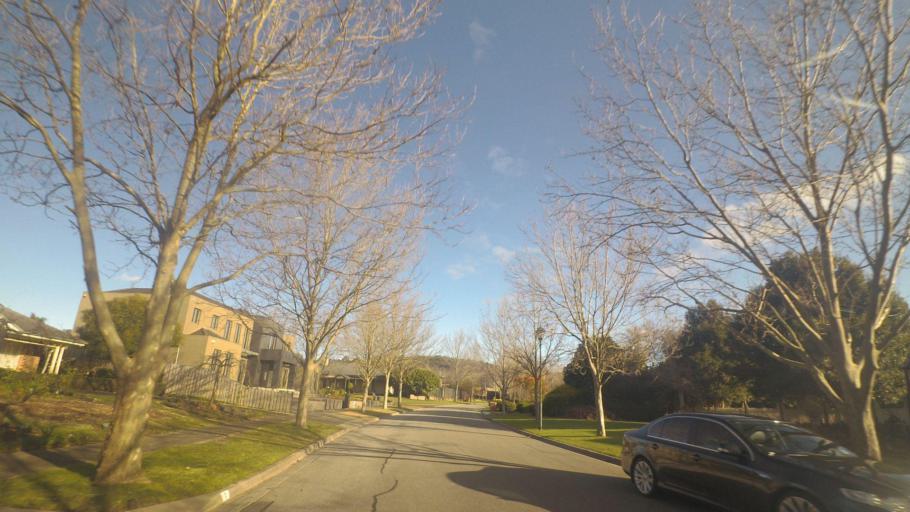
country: AU
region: Victoria
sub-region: Yarra Ranges
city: Lysterfield
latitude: -37.9188
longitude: 145.2868
